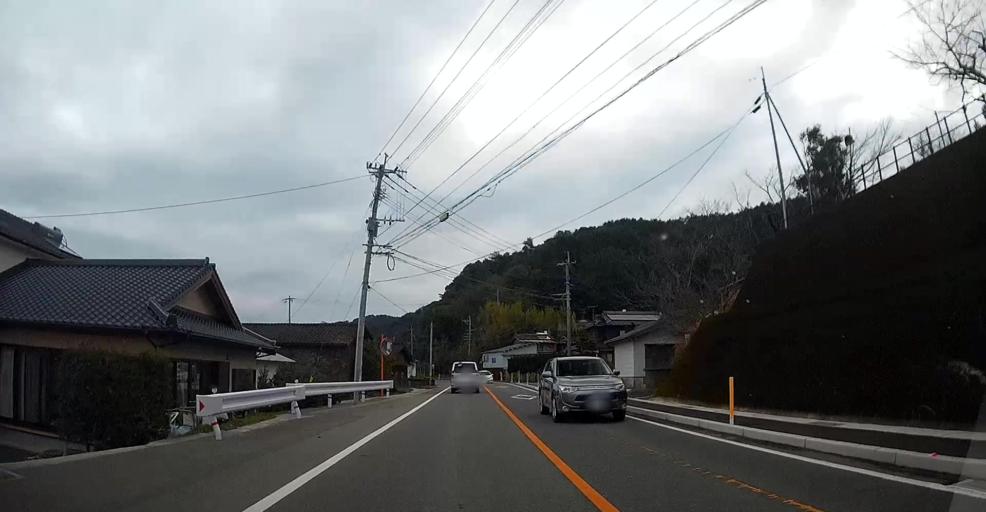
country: JP
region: Kumamoto
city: Hondo
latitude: 32.4835
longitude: 130.2779
